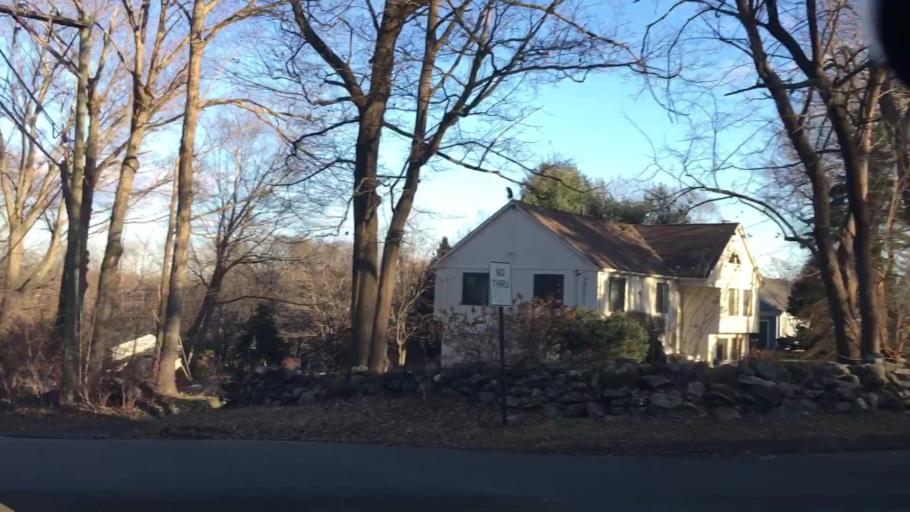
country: US
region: Connecticut
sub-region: Fairfield County
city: Newtown
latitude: 41.4198
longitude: -73.3058
